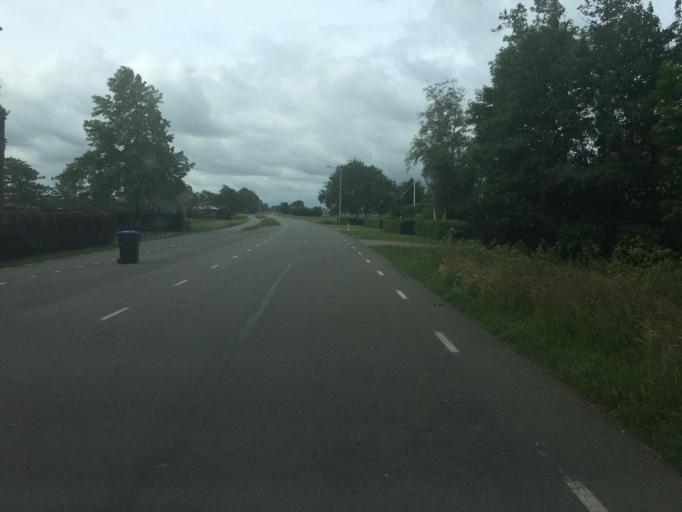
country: NL
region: Friesland
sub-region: Gemeente Lemsterland
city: Echtenerbrug
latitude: 52.8838
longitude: 5.8378
